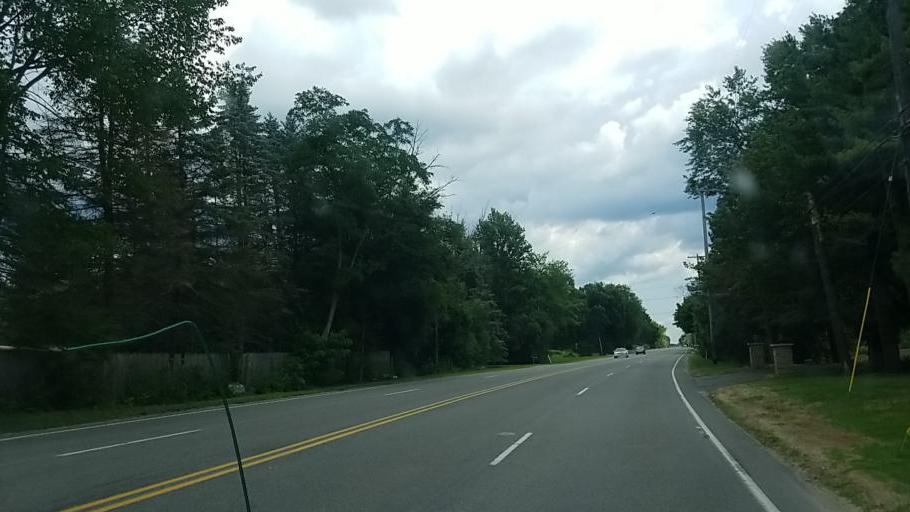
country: US
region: Michigan
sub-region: Kent County
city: East Grand Rapids
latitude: 42.9543
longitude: -85.5828
